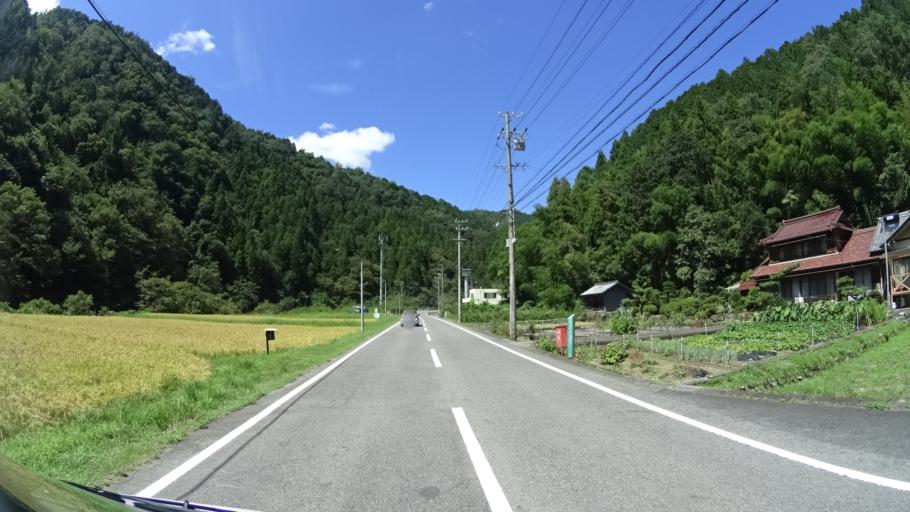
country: JP
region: Gifu
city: Minokamo
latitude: 35.5637
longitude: 137.1073
